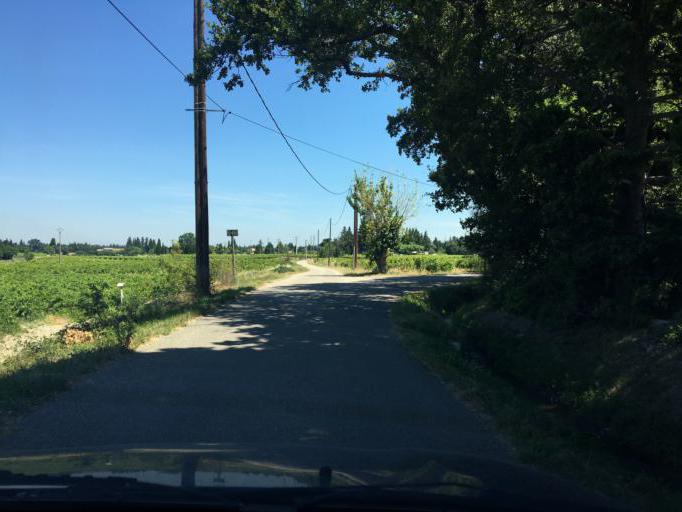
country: FR
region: Provence-Alpes-Cote d'Azur
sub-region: Departement du Vaucluse
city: Camaret-sur-Aigues
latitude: 44.1694
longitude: 4.8939
